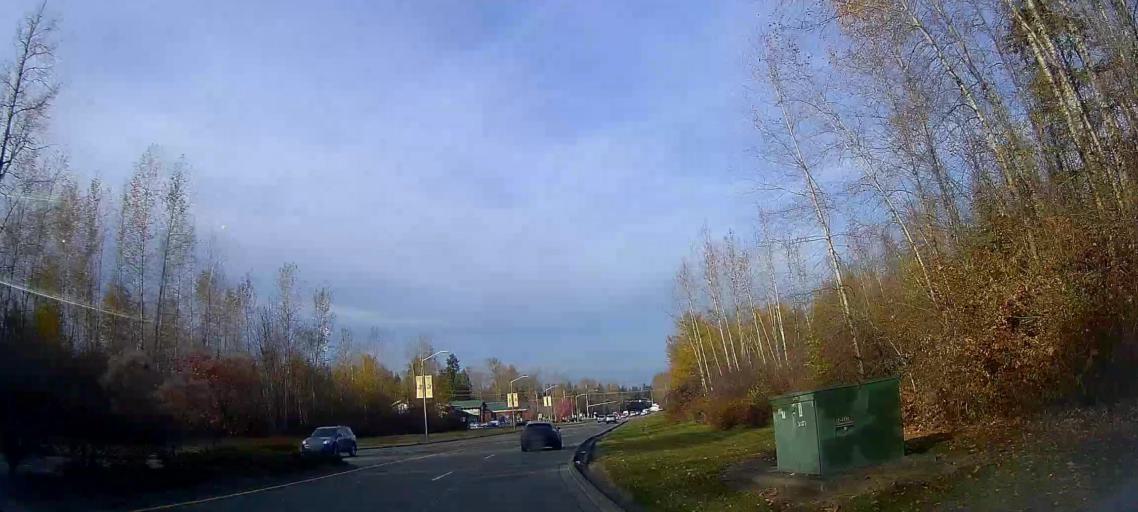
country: US
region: Washington
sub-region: Snohomish County
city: Marysville
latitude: 48.0975
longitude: -122.1918
